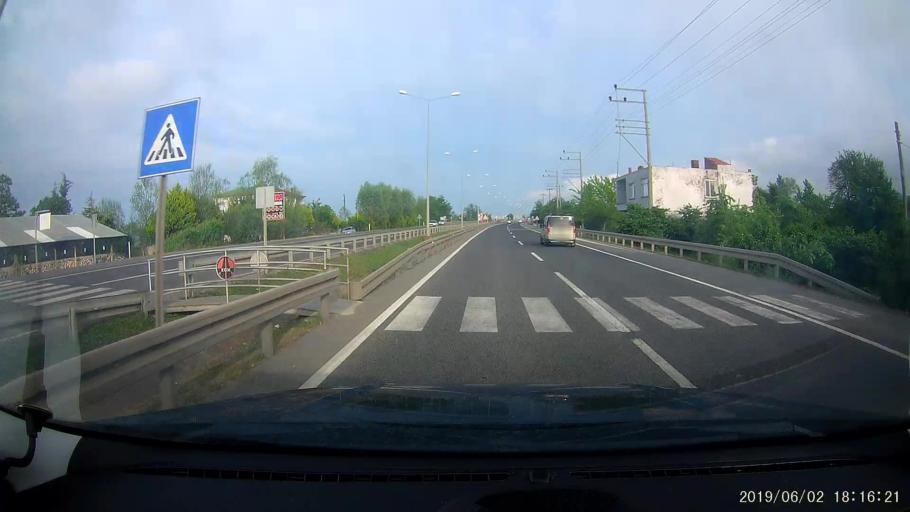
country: TR
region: Ordu
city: Unieh
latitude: 41.1013
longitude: 37.3969
